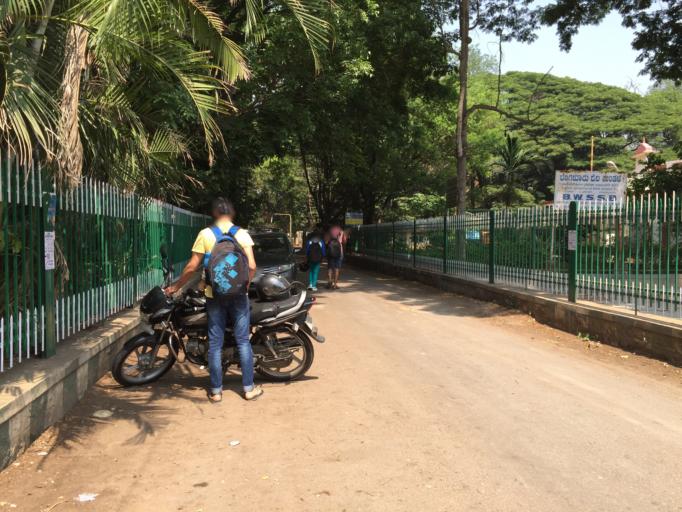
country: IN
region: Karnataka
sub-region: Bangalore Urban
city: Bangalore
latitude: 12.9426
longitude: 77.5766
